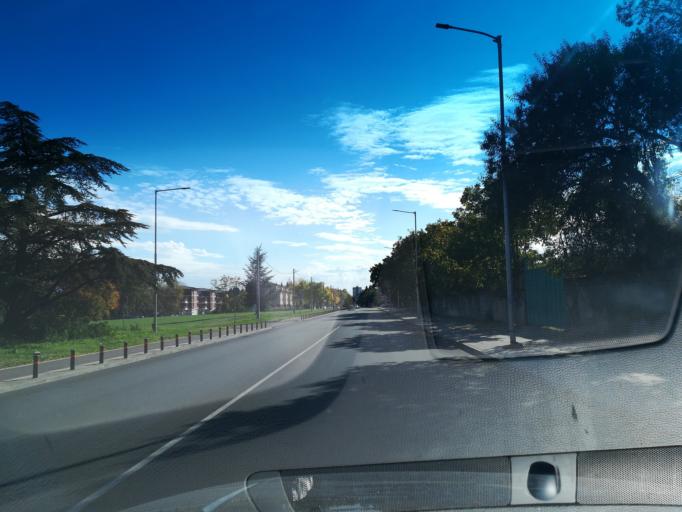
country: BG
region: Stara Zagora
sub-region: Obshtina Stara Zagora
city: Stara Zagora
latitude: 42.4407
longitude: 25.6351
